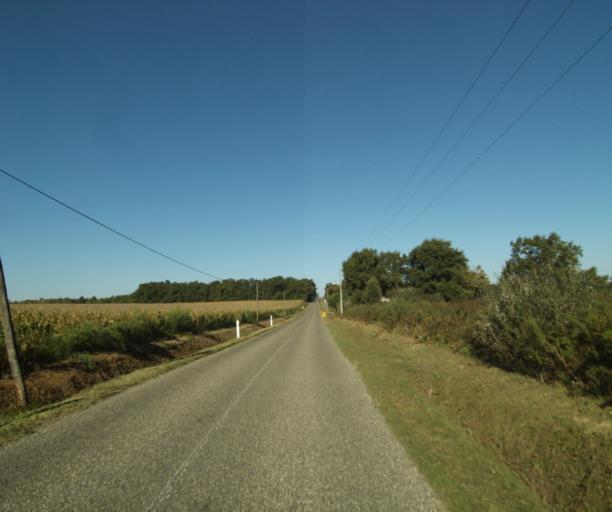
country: FR
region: Aquitaine
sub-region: Departement des Landes
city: Gabarret
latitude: 43.9533
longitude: -0.0113
